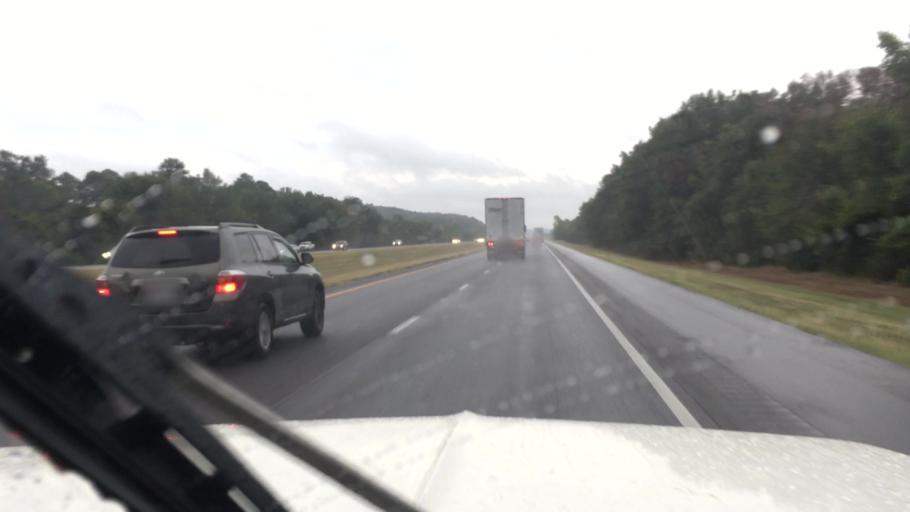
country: US
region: Alabama
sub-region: Morgan County
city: Falkville
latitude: 34.3989
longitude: -86.8972
